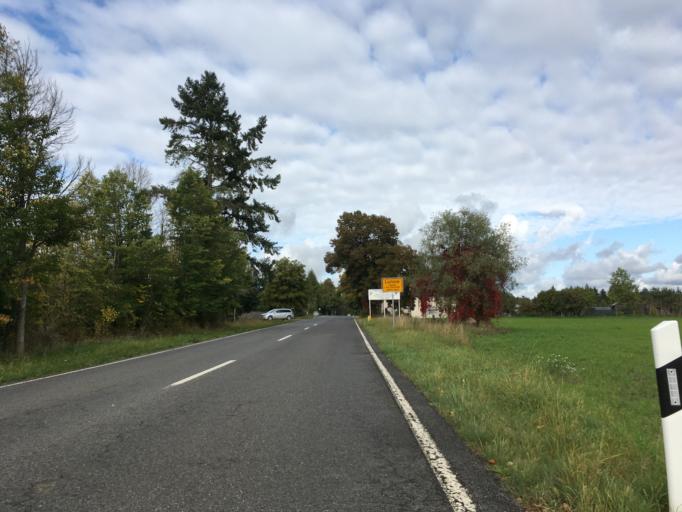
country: DE
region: Brandenburg
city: Oderberg
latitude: 52.9119
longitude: 14.1191
